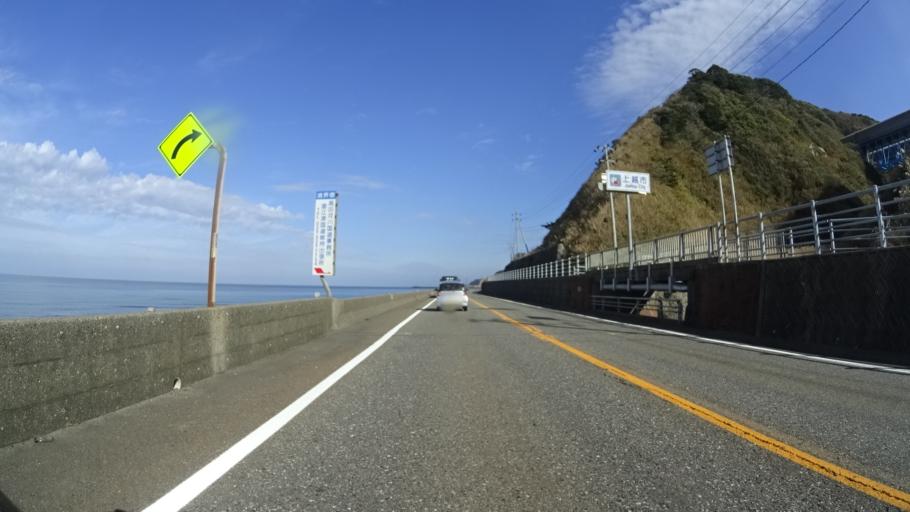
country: JP
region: Niigata
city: Joetsu
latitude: 37.1477
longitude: 138.0678
